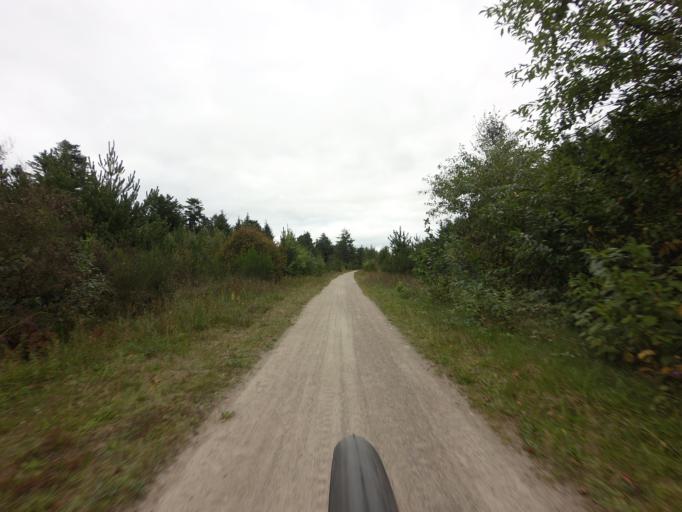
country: DK
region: South Denmark
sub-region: Billund Kommune
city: Grindsted
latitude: 55.7755
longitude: 8.9305
